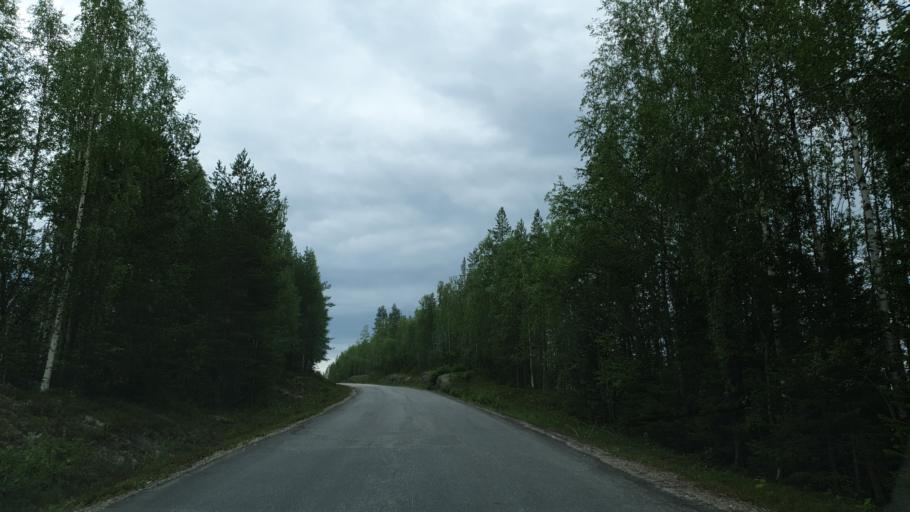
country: FI
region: Kainuu
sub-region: Kehys-Kainuu
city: Kuhmo
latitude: 64.3373
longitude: 29.3443
